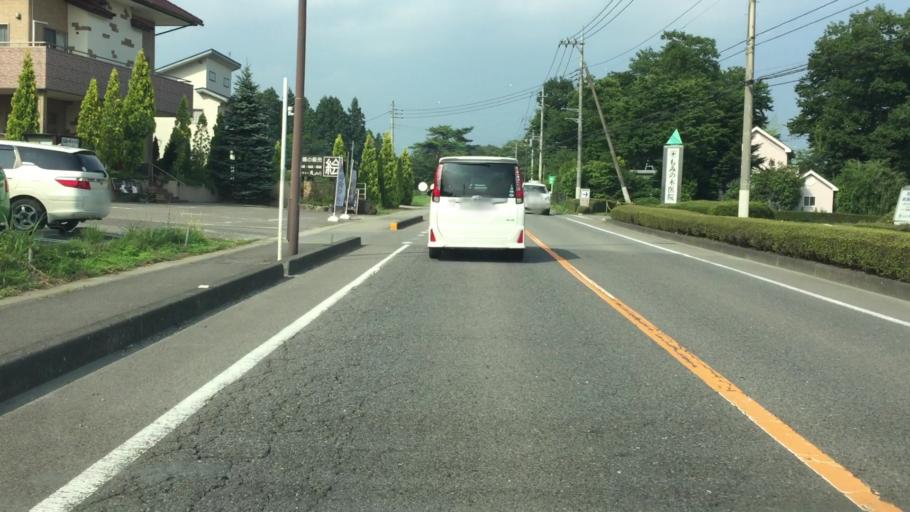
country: JP
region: Tochigi
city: Kuroiso
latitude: 37.0521
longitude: 140.0329
